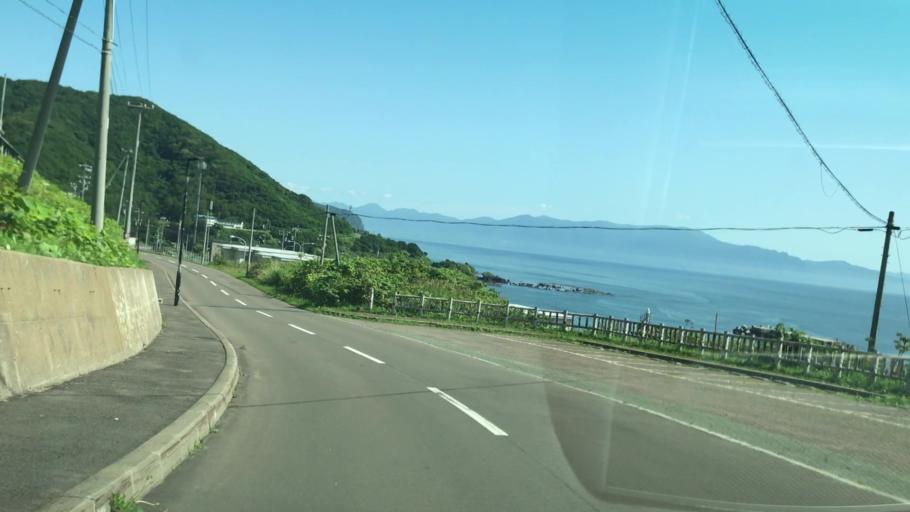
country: JP
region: Hokkaido
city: Iwanai
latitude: 43.1457
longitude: 140.4234
